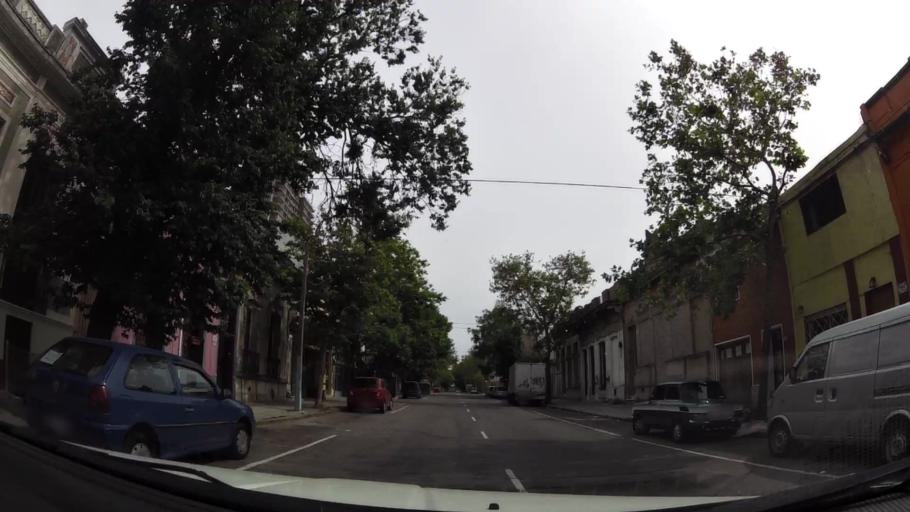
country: UY
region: Montevideo
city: Montevideo
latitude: -34.9130
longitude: -56.1861
